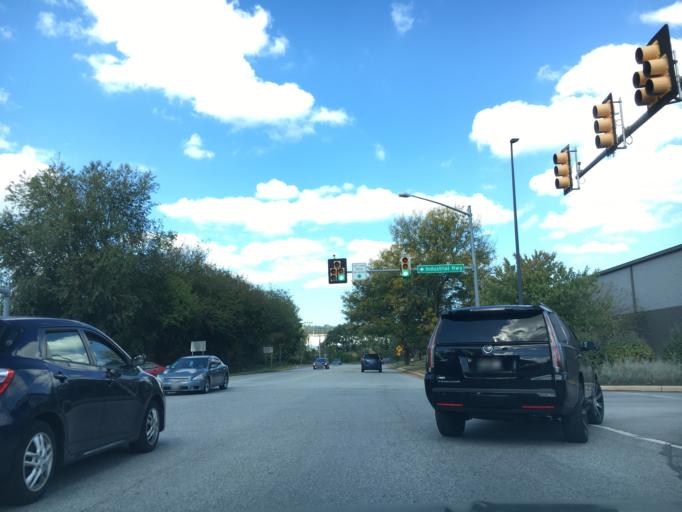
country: US
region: Pennsylvania
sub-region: York County
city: East York
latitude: 39.9797
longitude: -76.6749
